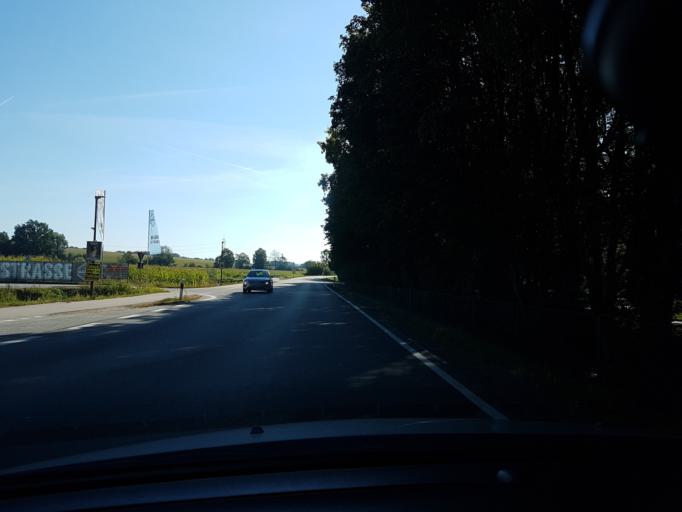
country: DE
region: Bavaria
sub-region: Upper Bavaria
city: Taufkirchen
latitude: 48.3464
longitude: 12.1373
